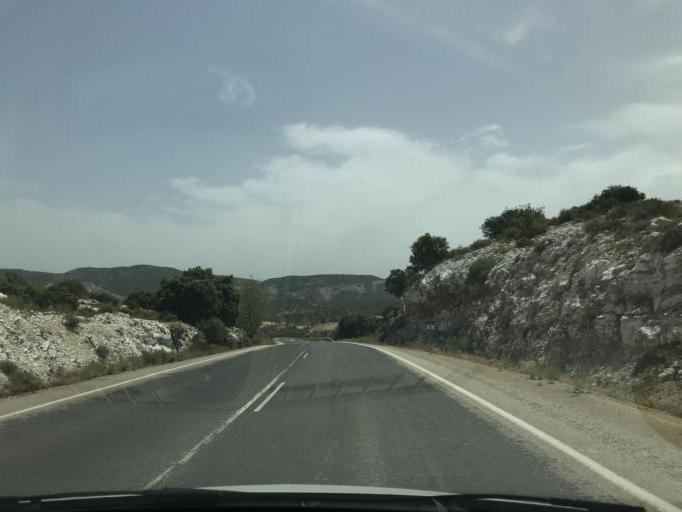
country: ES
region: Castille-La Mancha
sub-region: Provincia de Cuenca
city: La Frontera
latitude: 40.4020
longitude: -2.2304
